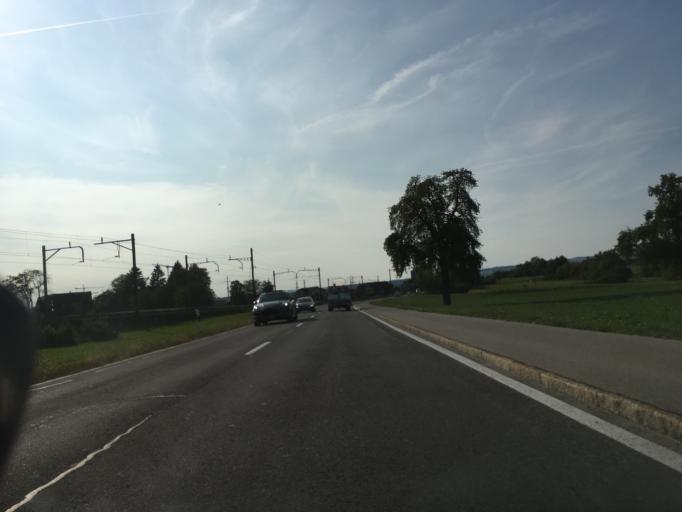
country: CH
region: Lucerne
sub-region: Lucerne-Land District
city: Meierskappel
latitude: 47.1445
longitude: 8.4506
